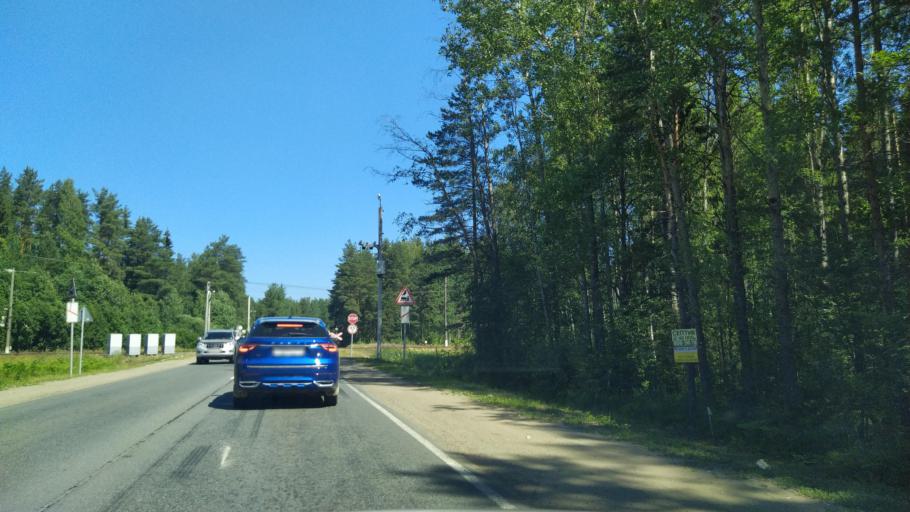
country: RU
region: Leningrad
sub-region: Volosovskiy Rayon
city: Shlissel'burg
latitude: 59.9459
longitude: 30.9852
